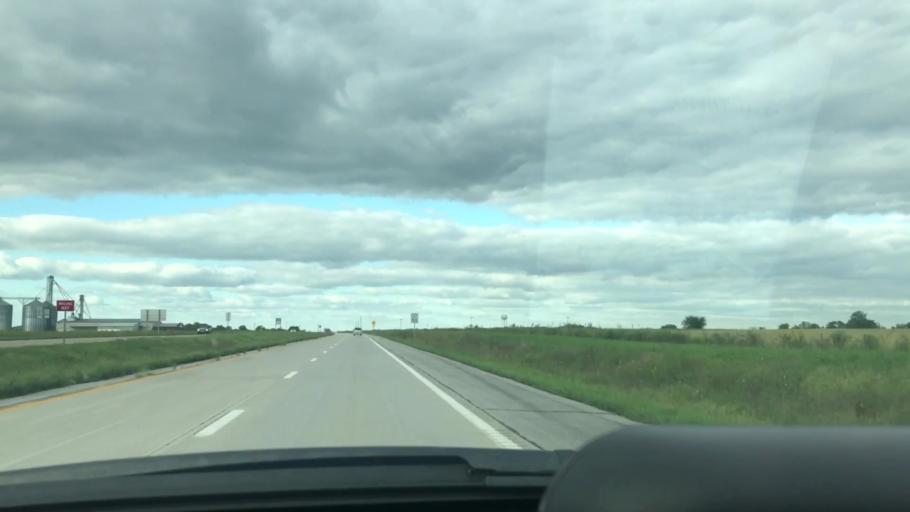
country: US
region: Missouri
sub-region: Benton County
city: Lincoln
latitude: 38.3777
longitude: -93.3367
